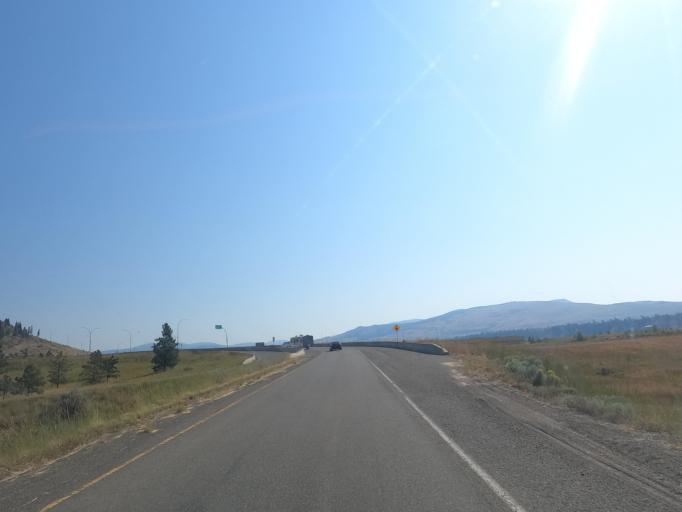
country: CA
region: British Columbia
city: Merritt
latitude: 50.1214
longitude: -120.7572
